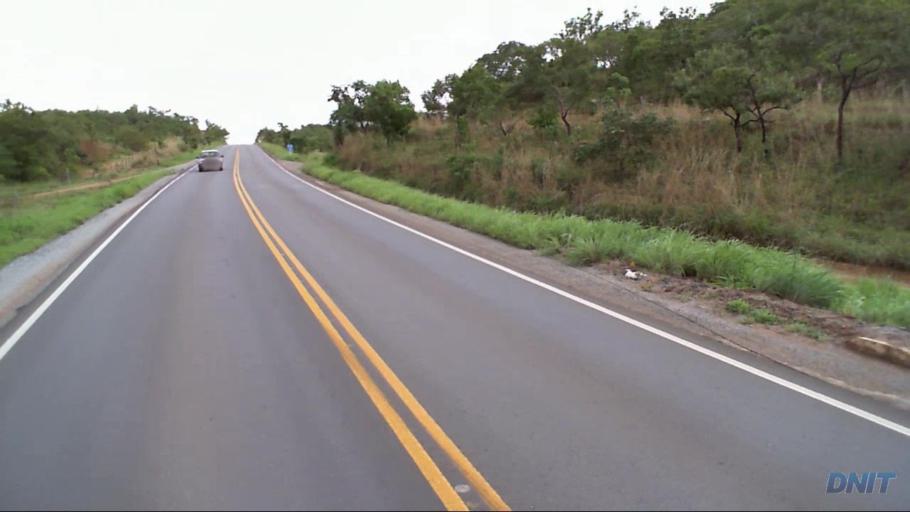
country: BR
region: Goias
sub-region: Padre Bernardo
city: Padre Bernardo
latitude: -15.2213
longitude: -48.2800
